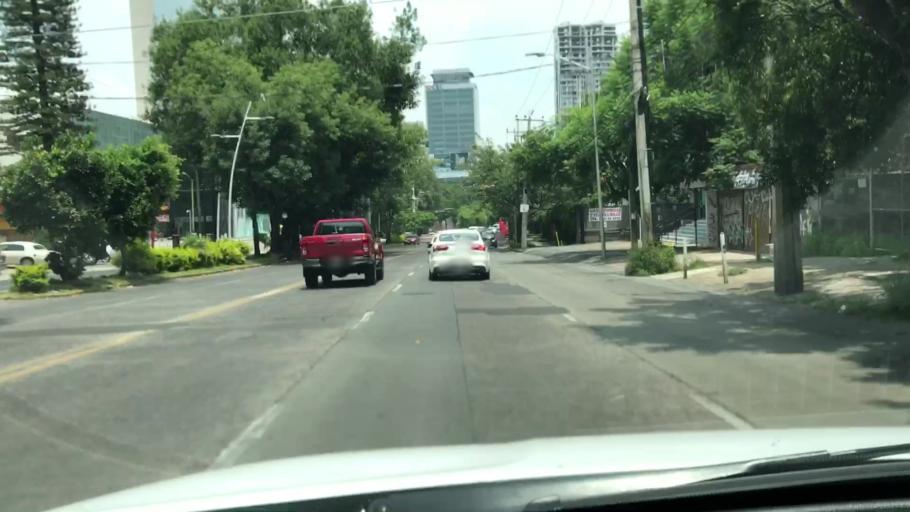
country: MX
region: Jalisco
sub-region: Zapopan
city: Zapopan
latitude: 20.7041
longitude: -103.3765
